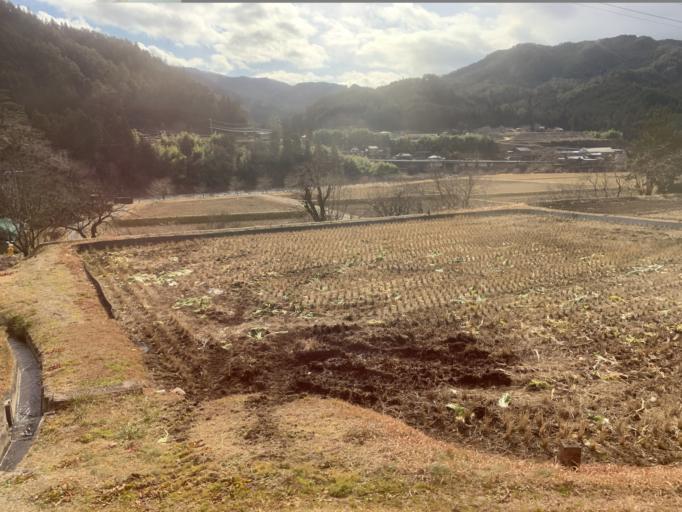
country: JP
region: Gifu
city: Takayama
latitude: 35.9280
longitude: 137.2227
